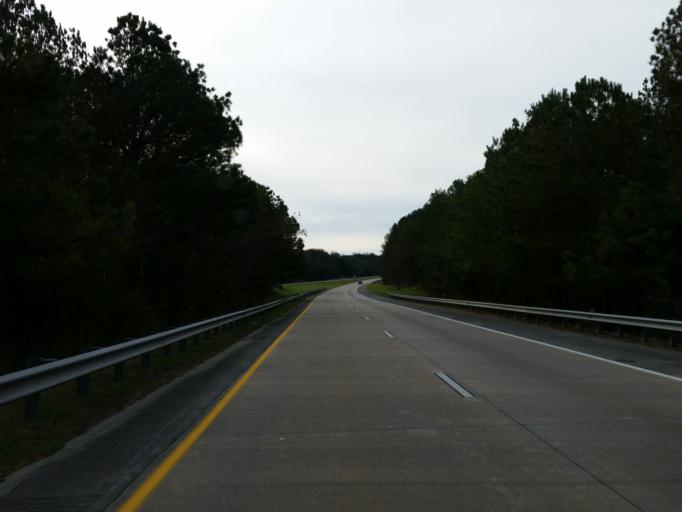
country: US
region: Georgia
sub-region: Cherokee County
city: Ball Ground
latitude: 34.3442
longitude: -84.3917
